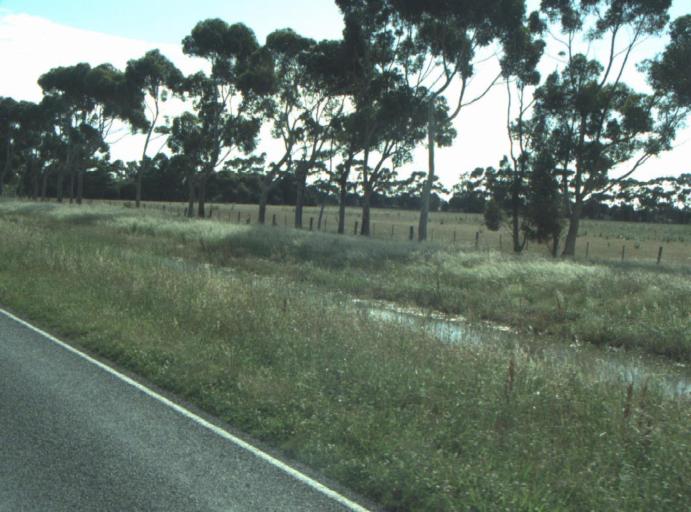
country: AU
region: Victoria
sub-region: Greater Geelong
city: Lara
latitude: -38.0169
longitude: 144.4483
